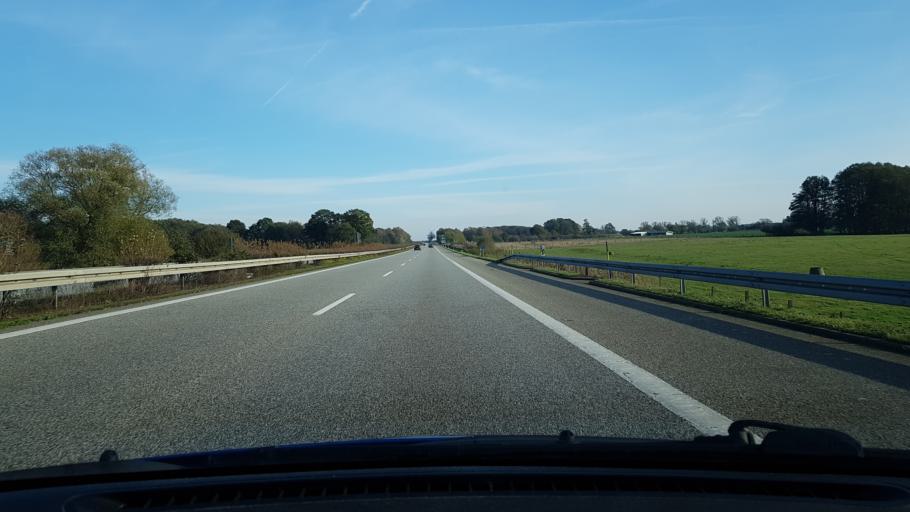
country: DE
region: Mecklenburg-Vorpommern
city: Wittenburg
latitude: 53.5013
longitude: 11.0500
